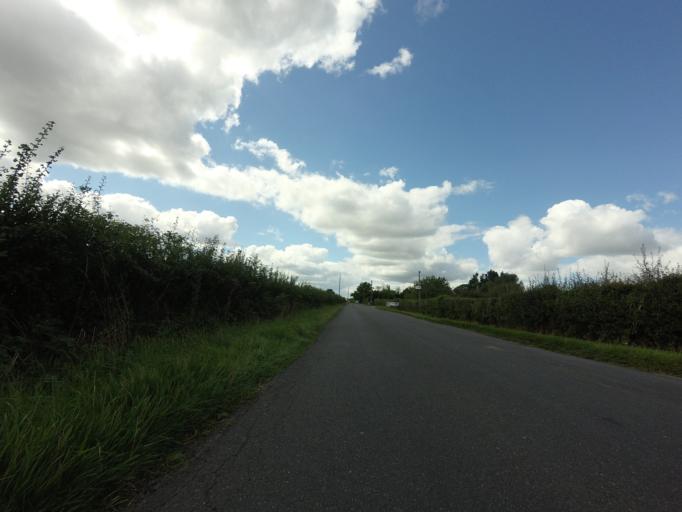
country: GB
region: England
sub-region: Kent
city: Staplehurst
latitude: 51.1528
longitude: 0.5469
